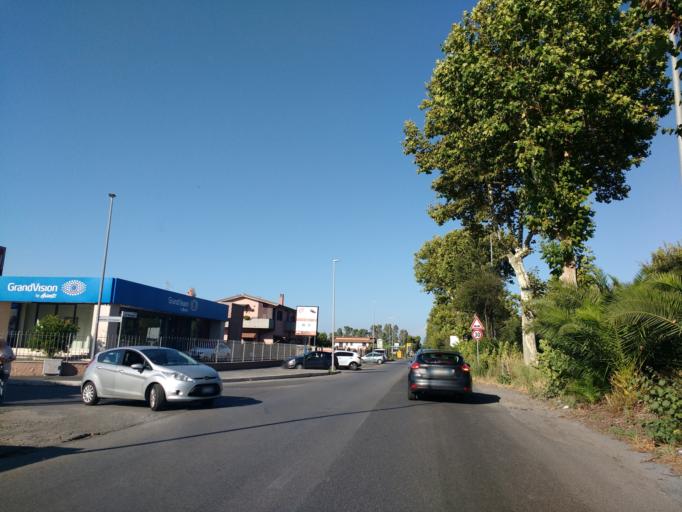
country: IT
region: Latium
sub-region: Citta metropolitana di Roma Capitale
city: Acilia-Castel Fusano-Ostia Antica
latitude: 41.7629
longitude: 12.3077
